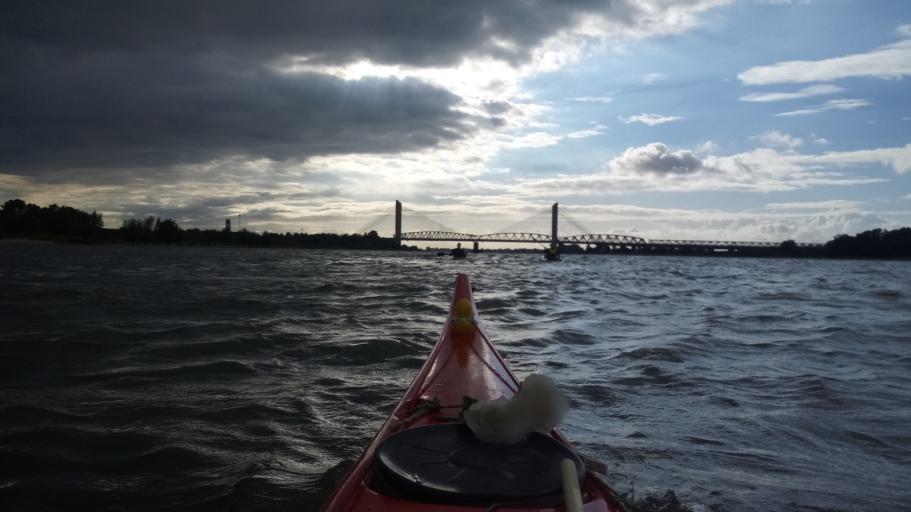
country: NL
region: Gelderland
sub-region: Gemeente Neerijnen
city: Neerijnen
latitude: 51.8197
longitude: 5.2775
